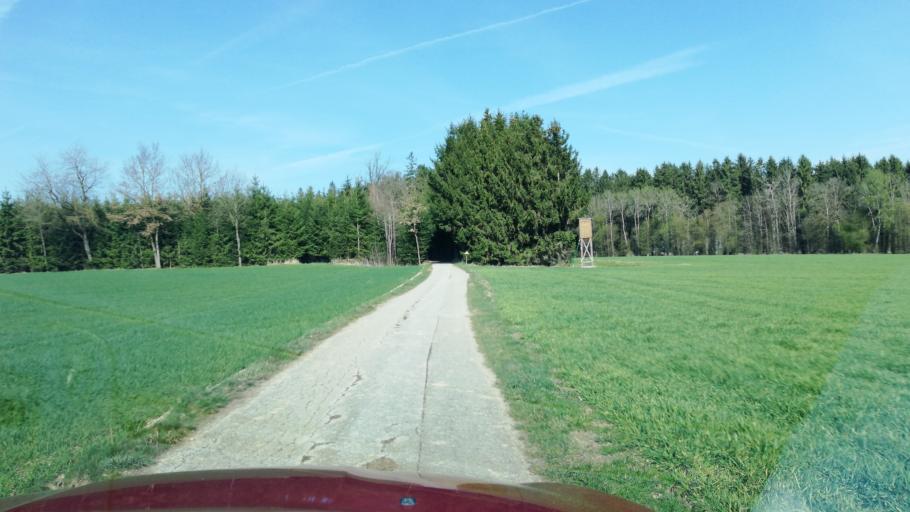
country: AT
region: Upper Austria
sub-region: Wels-Land
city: Sattledt
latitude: 48.0941
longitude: 14.0851
